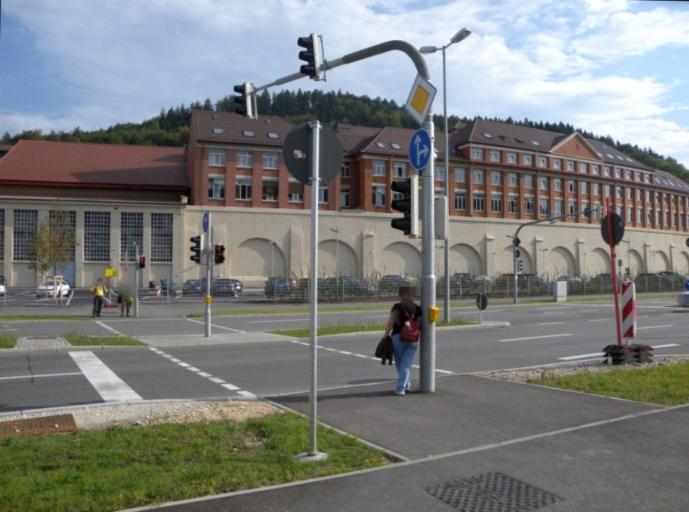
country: DE
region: Baden-Wuerttemberg
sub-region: Freiburg Region
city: Tuttlingen
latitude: 47.9800
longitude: 8.7997
